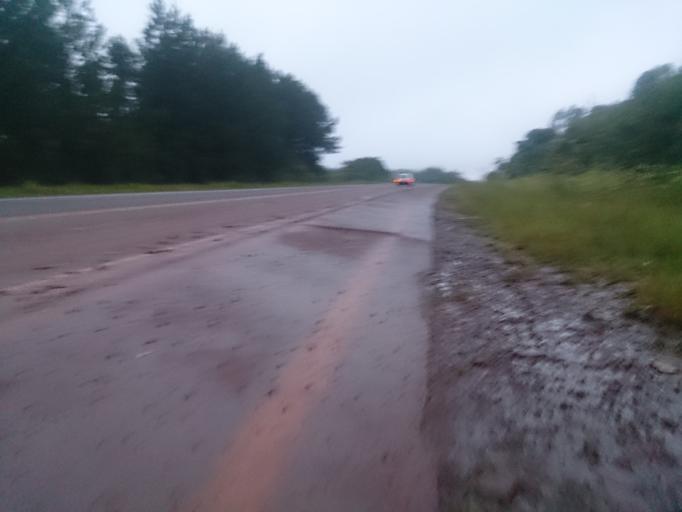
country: AR
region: Misiones
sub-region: Departamento de Obera
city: Obera
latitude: -27.4480
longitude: -55.0826
